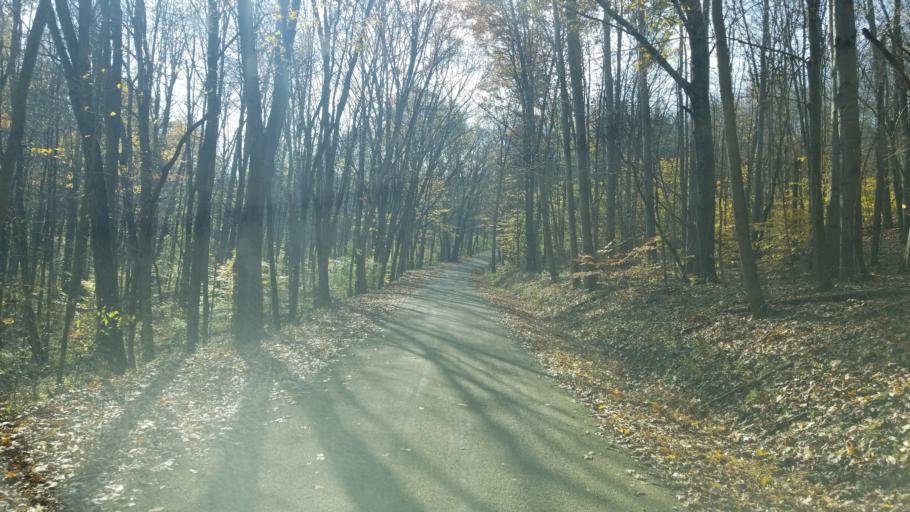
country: US
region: Ohio
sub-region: Sandusky County
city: Bellville
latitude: 40.6361
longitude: -82.4723
